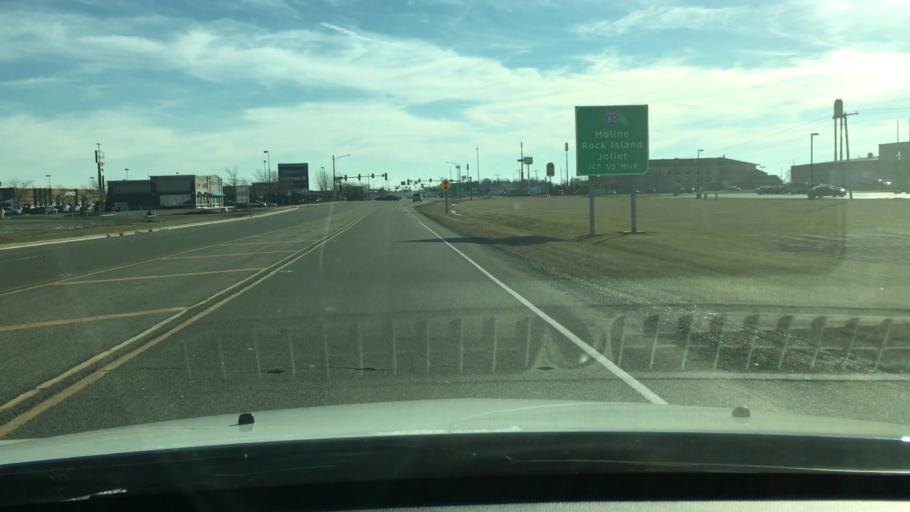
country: US
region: Illinois
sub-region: LaSalle County
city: Peru
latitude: 41.3741
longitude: -89.1256
